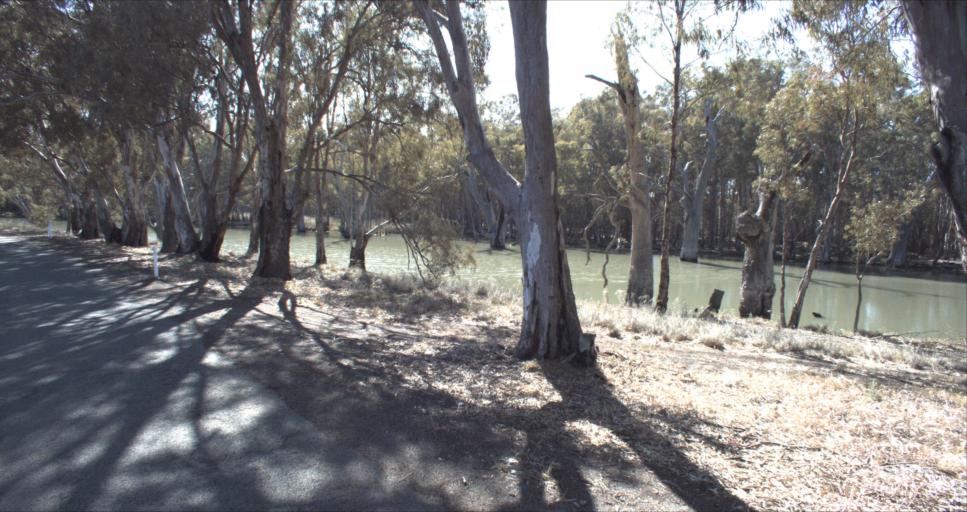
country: AU
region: New South Wales
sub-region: Leeton
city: Leeton
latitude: -34.6076
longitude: 146.2626
